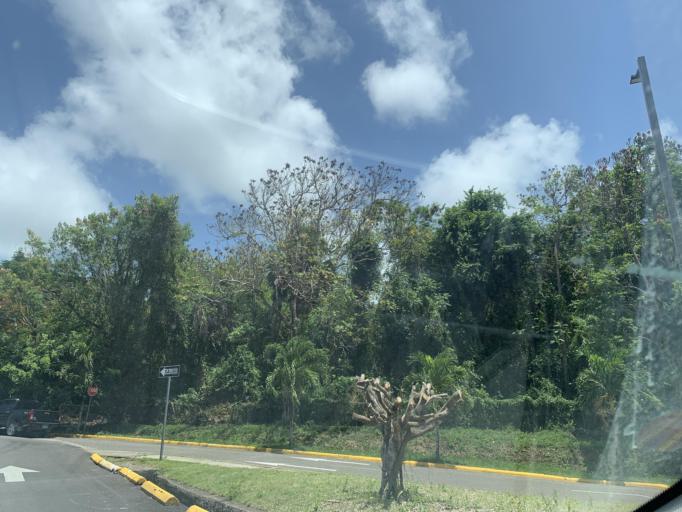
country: DO
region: Puerto Plata
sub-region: Puerto Plata
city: Puerto Plata
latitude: 19.7540
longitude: -70.5633
